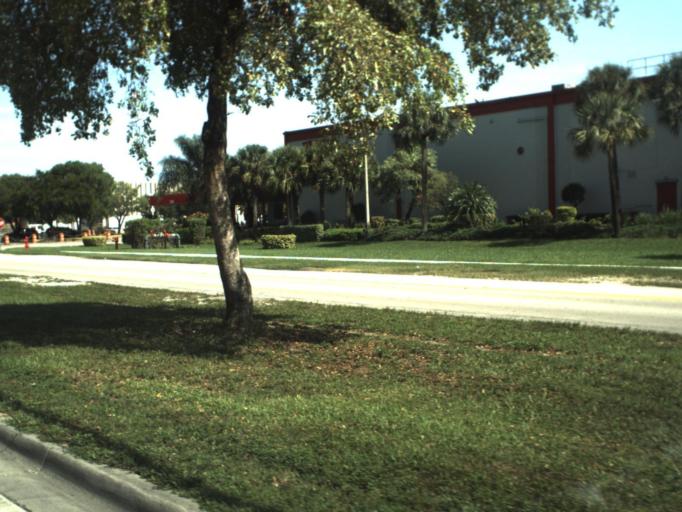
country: US
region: Florida
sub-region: Miami-Dade County
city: Norland
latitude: 25.9425
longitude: -80.2039
